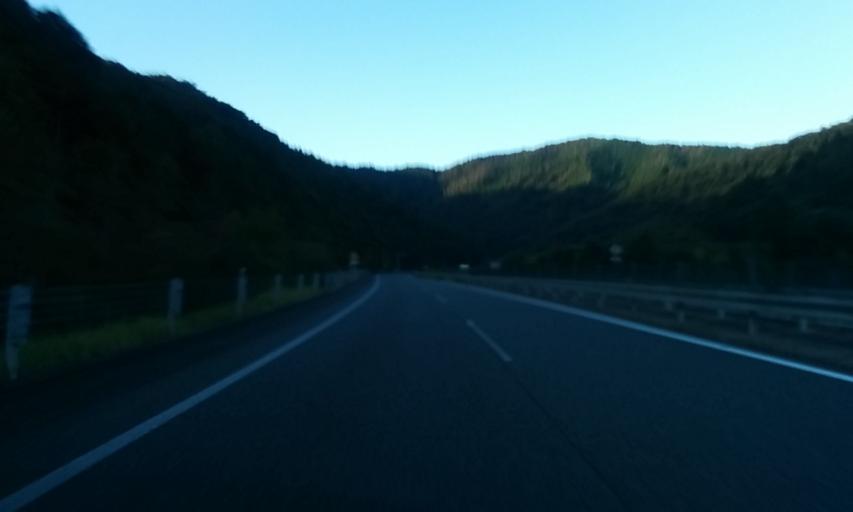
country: JP
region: Kyoto
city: Fukuchiyama
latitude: 35.2076
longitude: 135.1643
